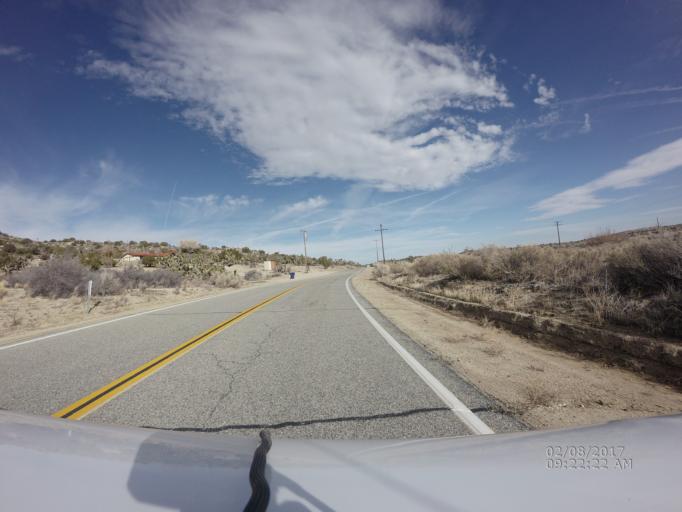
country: US
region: California
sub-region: Los Angeles County
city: Littlerock
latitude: 34.4512
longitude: -117.9016
